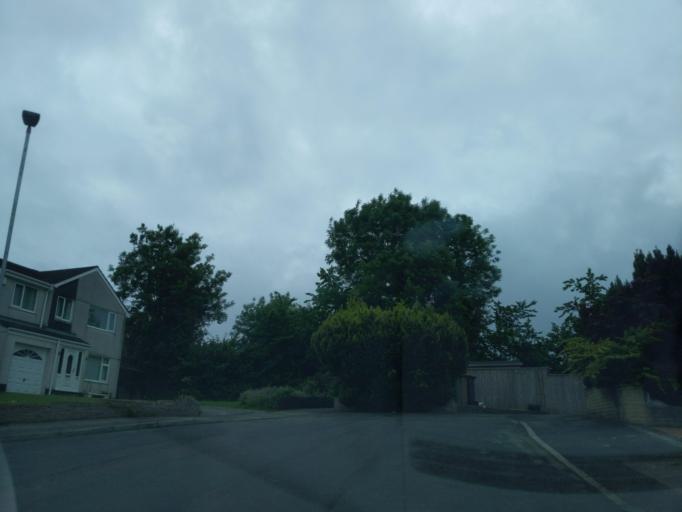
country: GB
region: England
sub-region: Devon
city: Plympton
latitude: 50.3918
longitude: -4.0344
